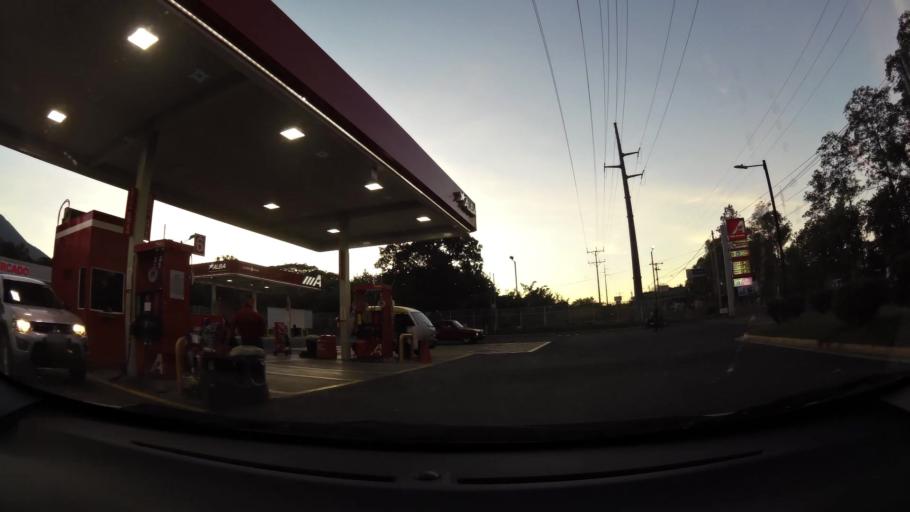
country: SV
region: San Miguel
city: Moncagua
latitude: 13.5061
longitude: -88.2327
